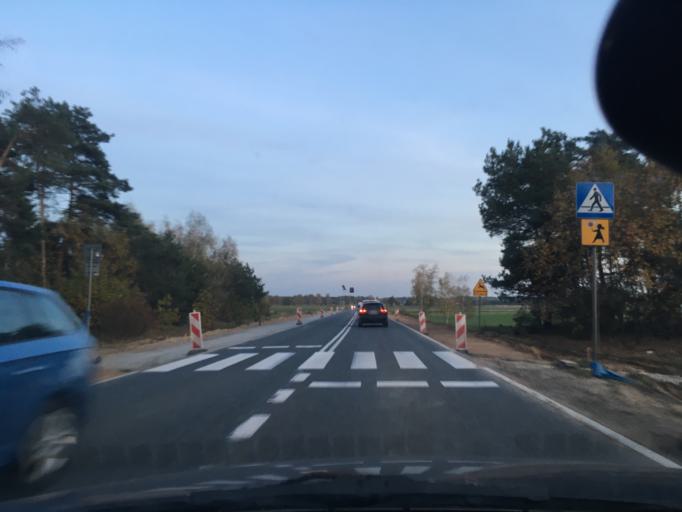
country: PL
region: Masovian Voivodeship
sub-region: Powiat plocki
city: Wyszogrod
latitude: 52.3619
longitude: 20.1982
